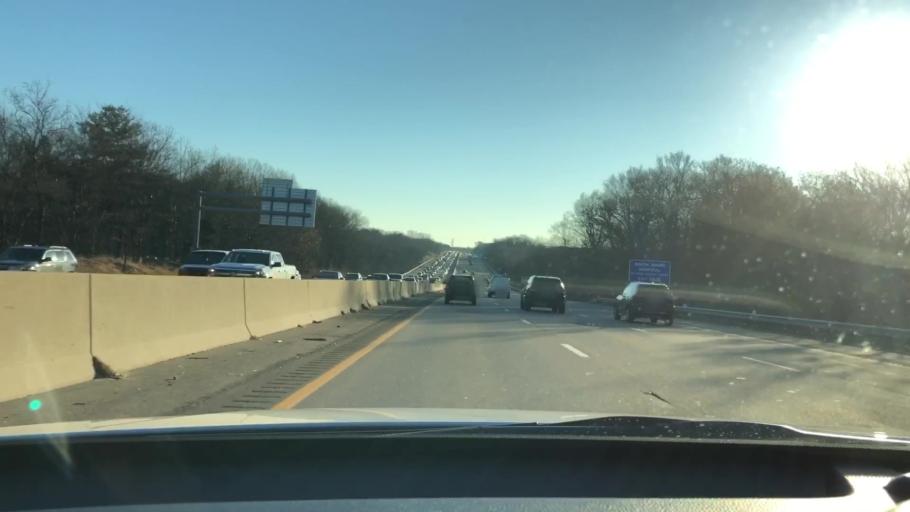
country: US
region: Massachusetts
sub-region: Norfolk County
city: Braintree
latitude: 42.2027
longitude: -70.9826
